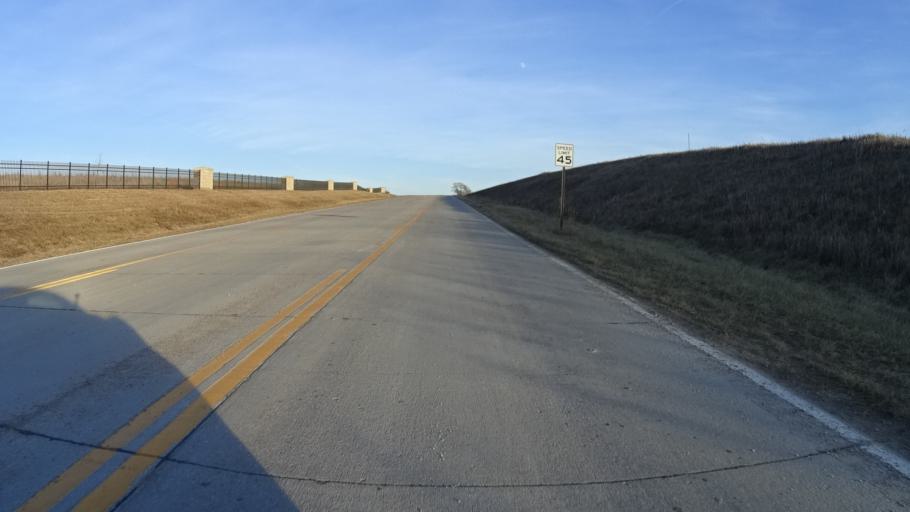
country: US
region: Nebraska
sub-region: Sarpy County
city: Springfield
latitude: 41.1325
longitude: -96.1382
